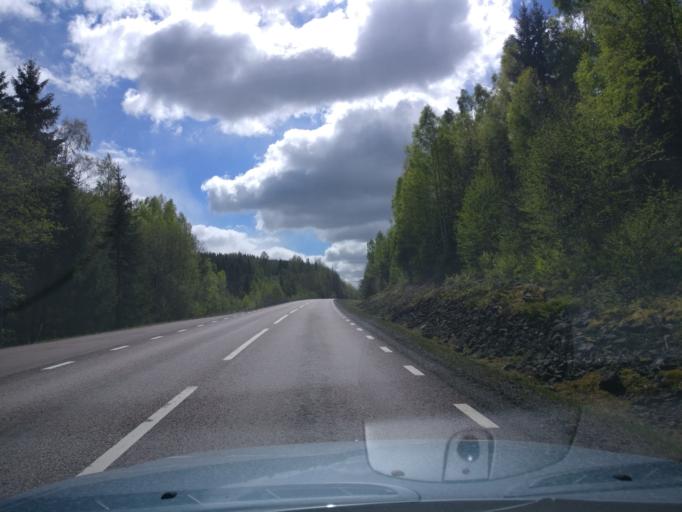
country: SE
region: Vaermland
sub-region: Karlstads Kommun
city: Molkom
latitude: 59.6585
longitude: 13.7097
